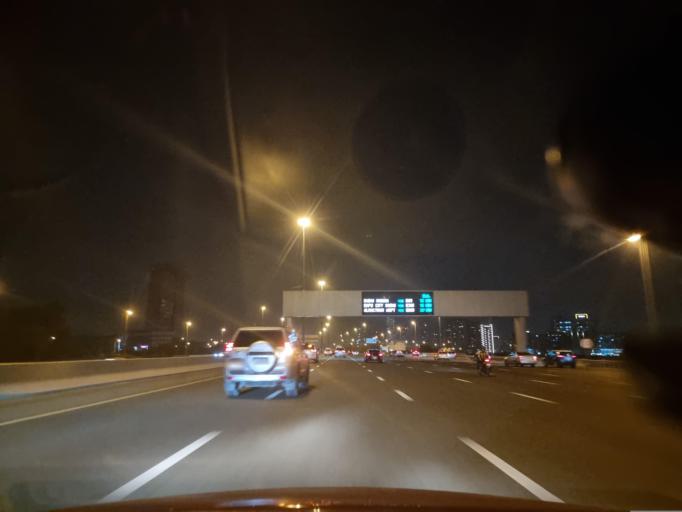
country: AE
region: Dubai
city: Dubai
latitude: 25.0555
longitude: 55.2367
